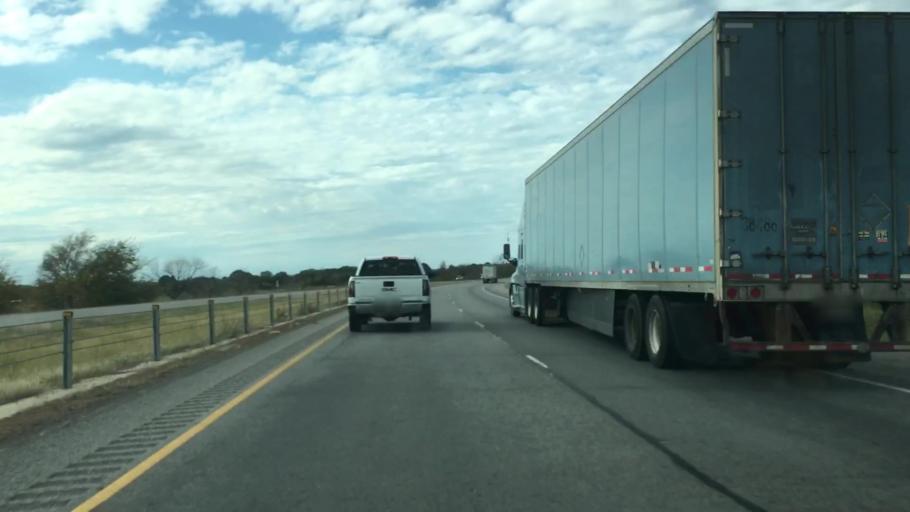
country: US
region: Arkansas
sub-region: Conway County
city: Morrilton
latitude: 35.1956
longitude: -92.7990
